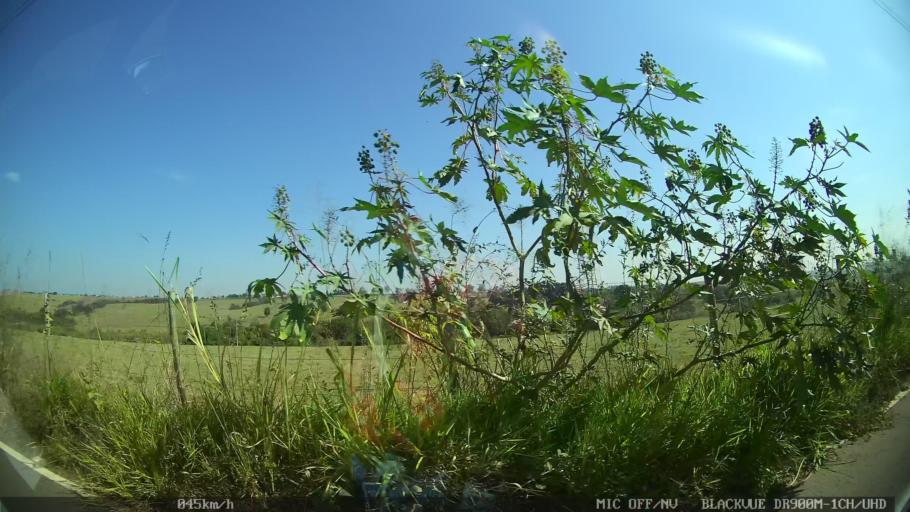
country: BR
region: Sao Paulo
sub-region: Valinhos
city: Valinhos
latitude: -23.0241
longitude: -47.0876
